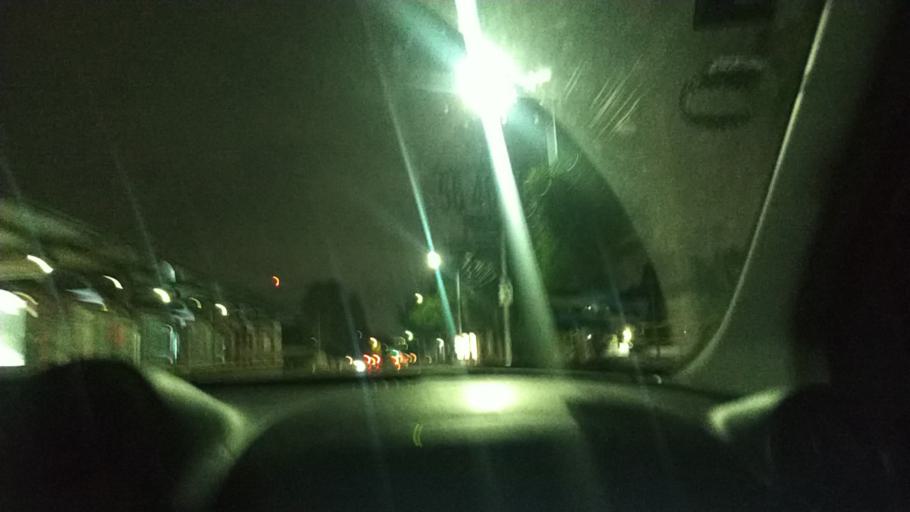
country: MX
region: Mexico
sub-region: Tultitlan
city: Fuentes del Valle
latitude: 19.6282
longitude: -99.1398
